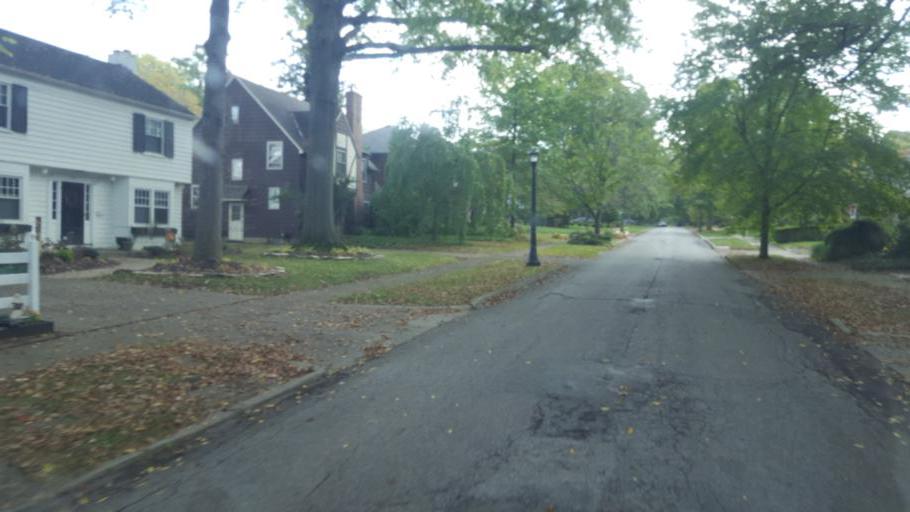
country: US
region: Ohio
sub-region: Franklin County
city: Worthington
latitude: 40.0381
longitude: -83.0084
